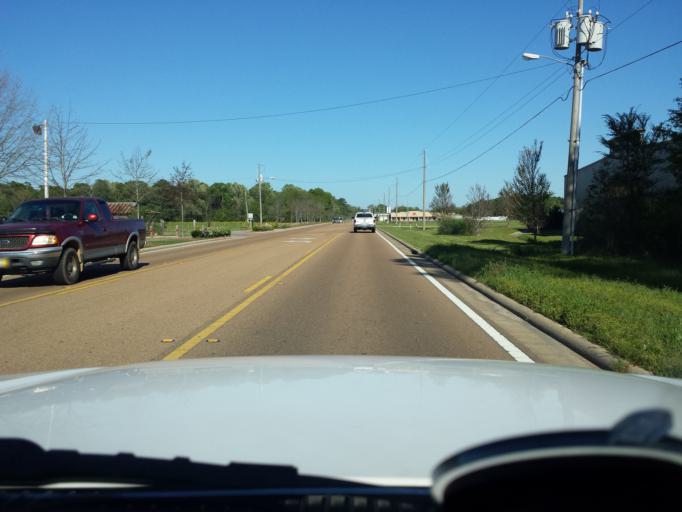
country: US
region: Mississippi
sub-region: Rankin County
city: Flowood
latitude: 32.3416
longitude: -90.0856
